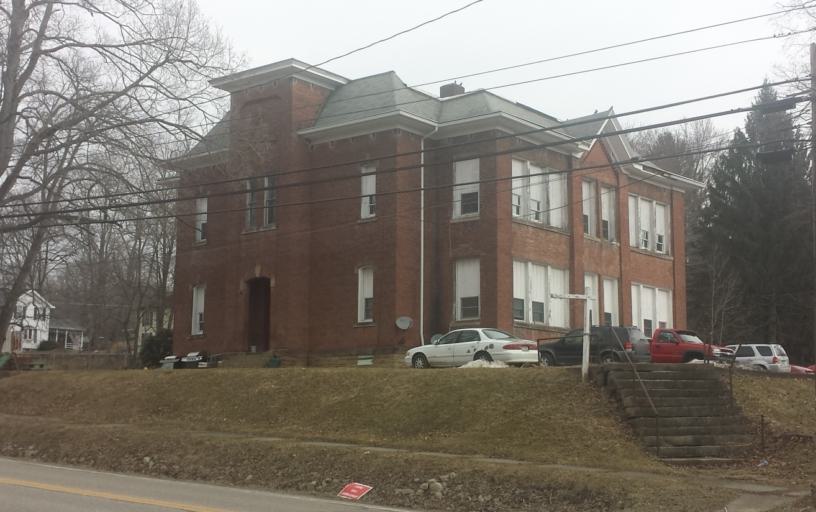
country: US
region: Pennsylvania
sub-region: Mercer County
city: Greenville
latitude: 41.4871
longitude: -80.4375
